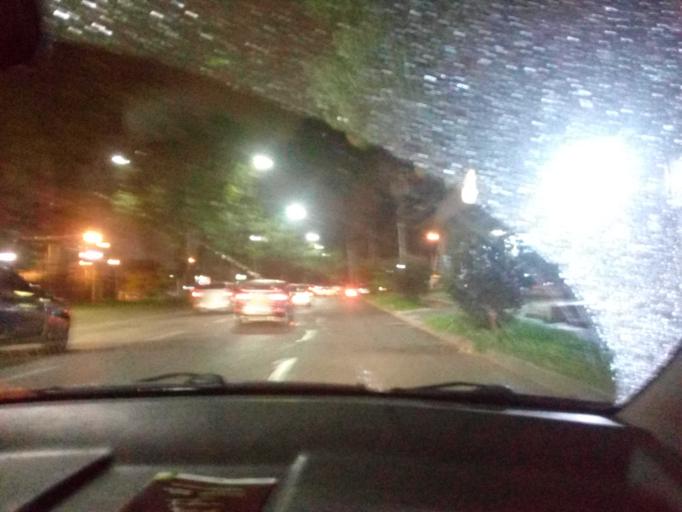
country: CO
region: Antioquia
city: Envigado
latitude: 6.1808
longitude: -75.5872
